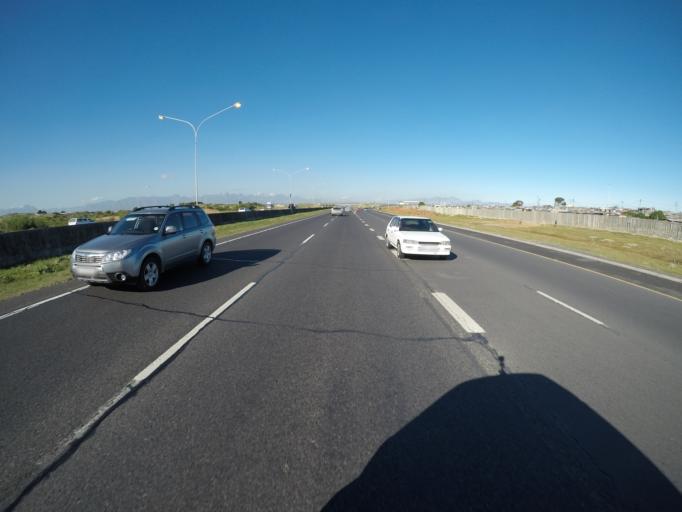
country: ZA
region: Western Cape
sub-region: City of Cape Town
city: Lansdowne
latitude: -34.0101
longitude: 18.6537
